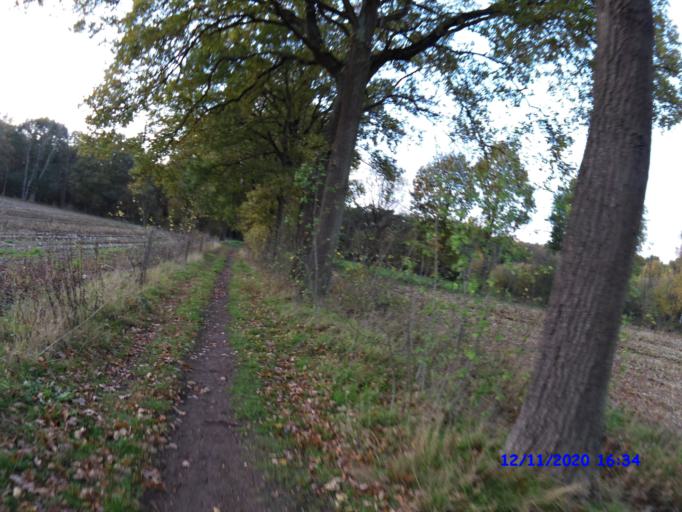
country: BE
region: Flanders
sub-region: Provincie Antwerpen
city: Geel
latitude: 51.1899
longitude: 5.0481
